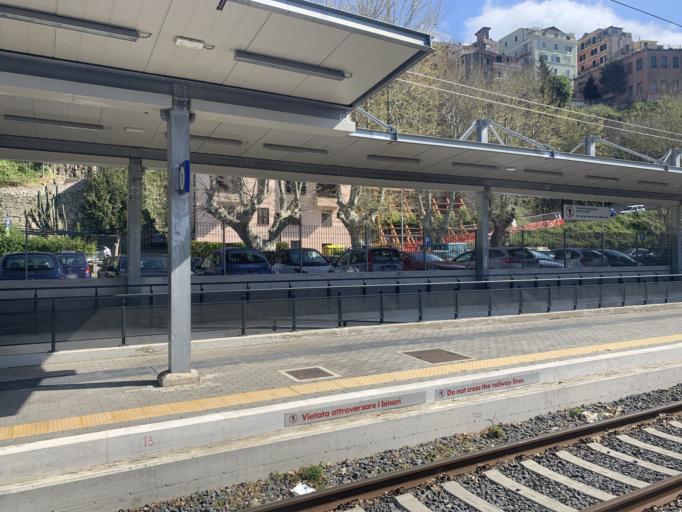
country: IT
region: Latium
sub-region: Citta metropolitana di Roma Capitale
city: Castel Gandolfo
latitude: 41.7690
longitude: 12.6564
